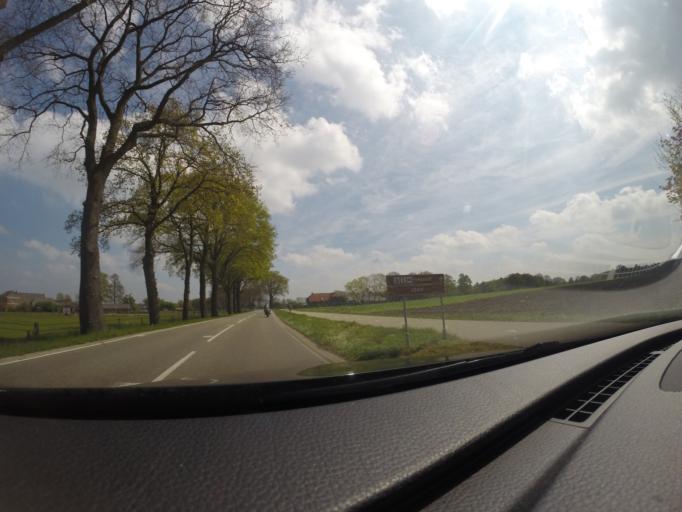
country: NL
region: Gelderland
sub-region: Berkelland
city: Neede
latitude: 52.1120
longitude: 6.5881
